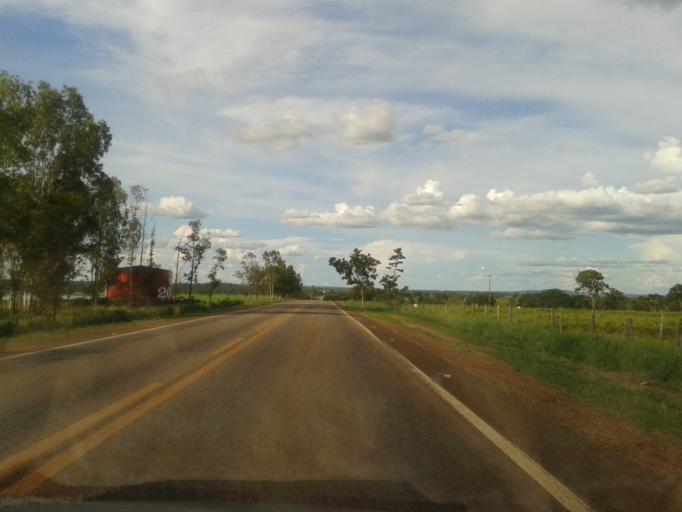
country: BR
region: Goias
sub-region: Crixas
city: Crixas
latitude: -14.2480
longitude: -50.3965
